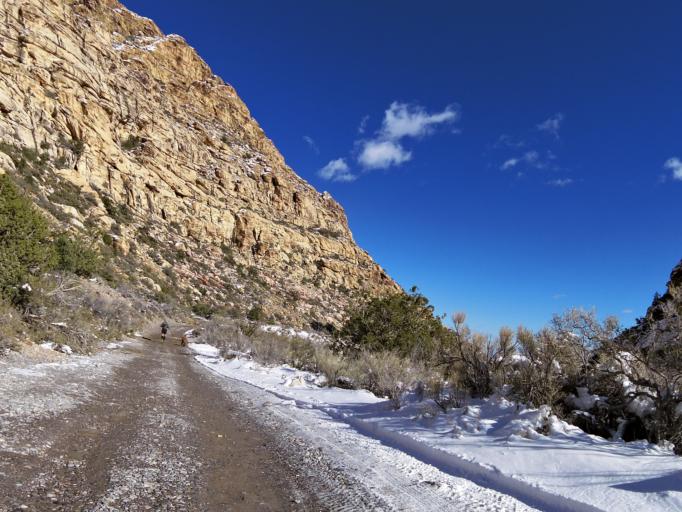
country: US
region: Nevada
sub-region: Clark County
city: Summerlin South
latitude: 36.1635
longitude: -115.5041
